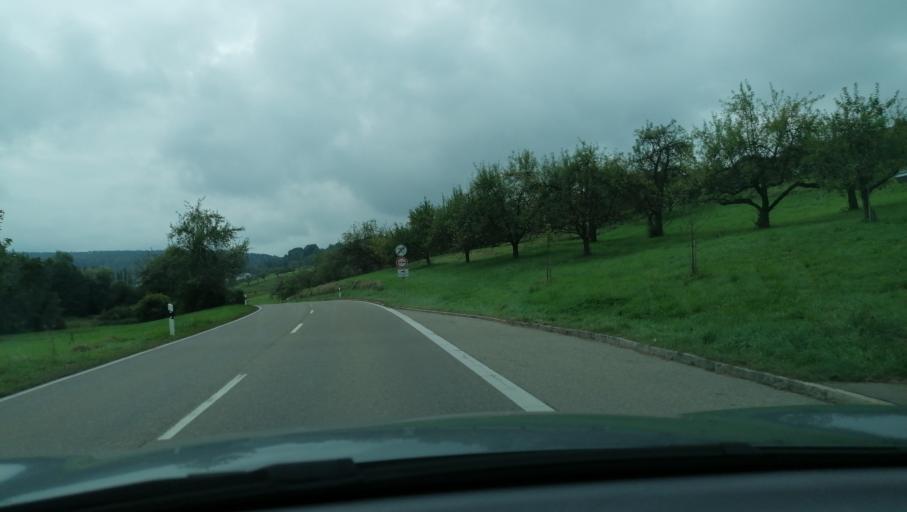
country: DE
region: Baden-Wuerttemberg
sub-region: Regierungsbezirk Stuttgart
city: Winnenden
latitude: 48.8548
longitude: 9.4404
